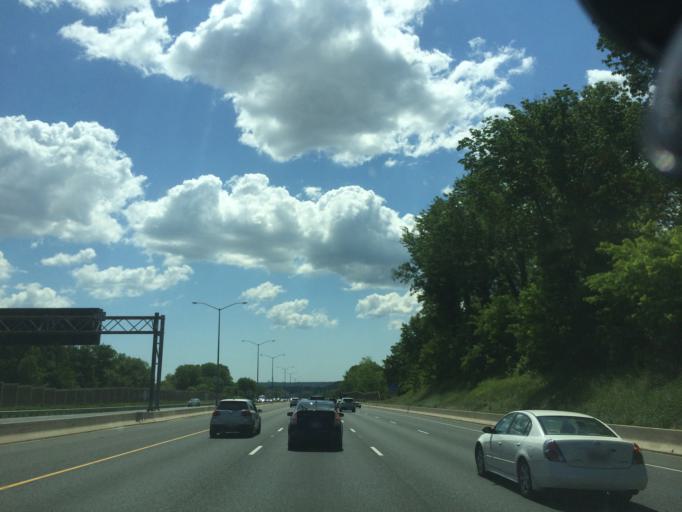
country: US
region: Maryland
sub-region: Baltimore County
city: Charlestown
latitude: 39.2660
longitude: -76.7135
